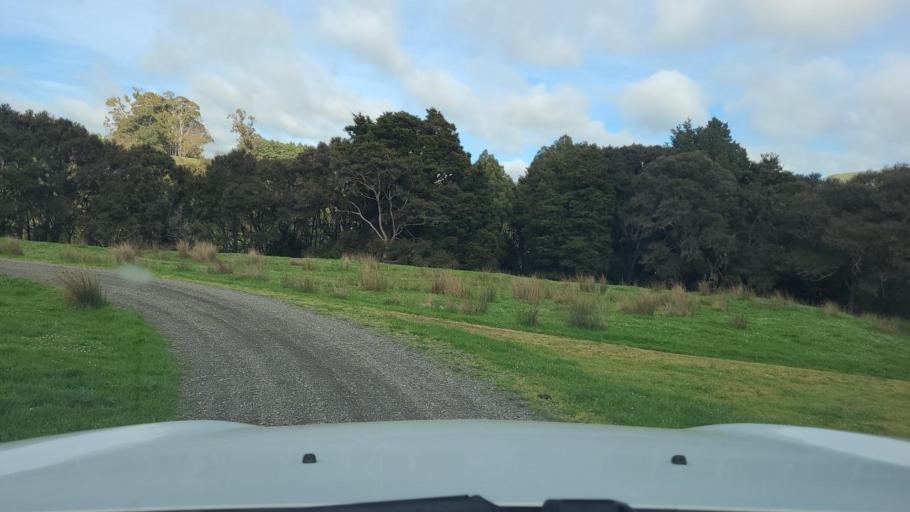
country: NZ
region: Wellington
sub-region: South Wairarapa District
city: Waipawa
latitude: -41.2600
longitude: 175.6866
